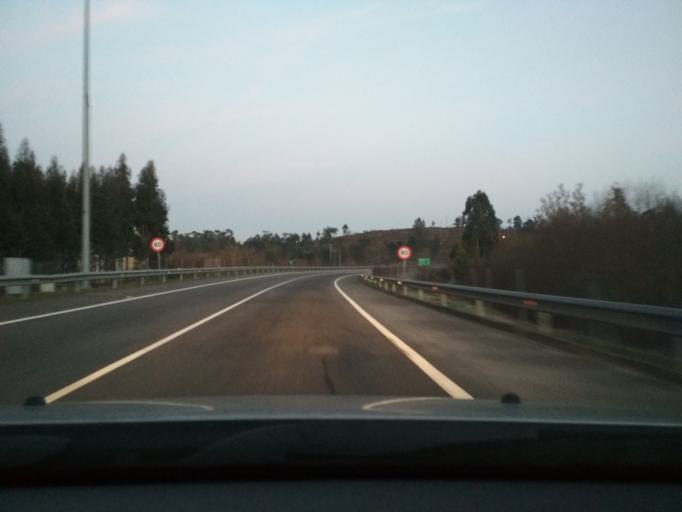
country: ES
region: Galicia
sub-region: Provincia da Coruna
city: Santiago de Compostela
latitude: 42.8361
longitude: -8.5905
